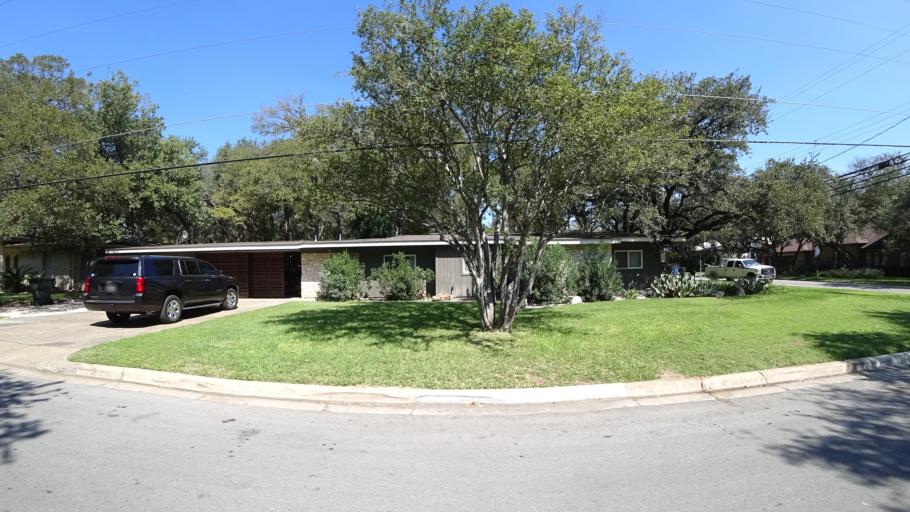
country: US
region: Texas
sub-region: Travis County
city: Rollingwood
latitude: 30.2764
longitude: -97.7919
